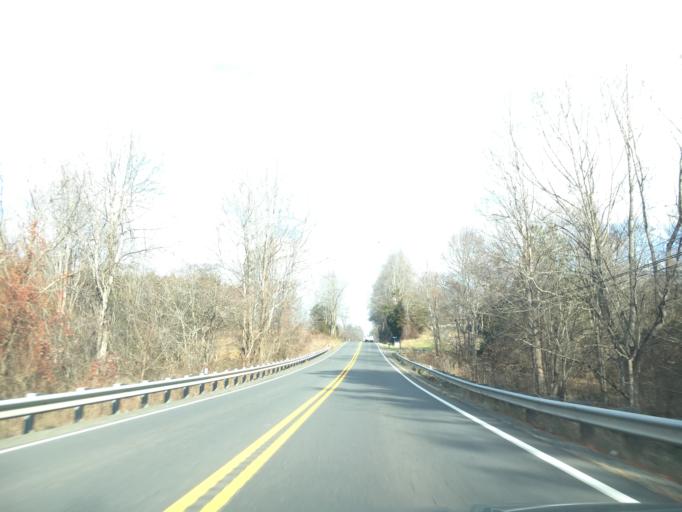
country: US
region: Virginia
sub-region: Culpeper County
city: Culpeper
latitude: 38.6003
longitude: -77.9599
